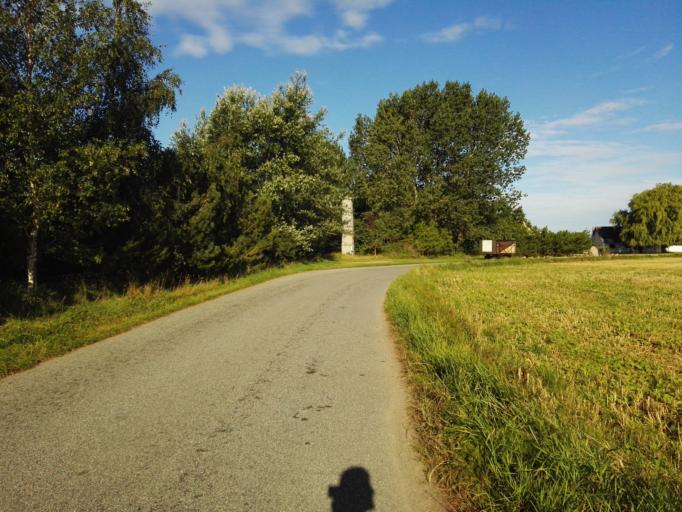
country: DK
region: Zealand
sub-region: Odsherred Kommune
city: Nykobing Sjaelland
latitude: 55.9590
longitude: 11.7655
